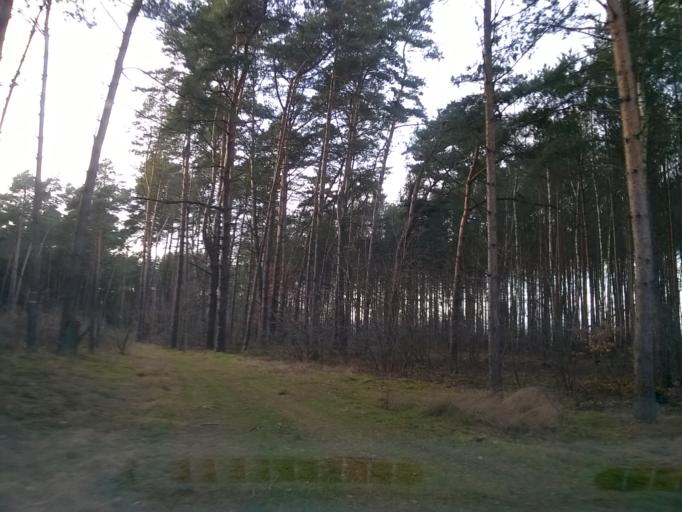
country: PL
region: Kujawsko-Pomorskie
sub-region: Powiat nakielski
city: Kcynia
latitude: 53.0277
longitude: 17.4458
